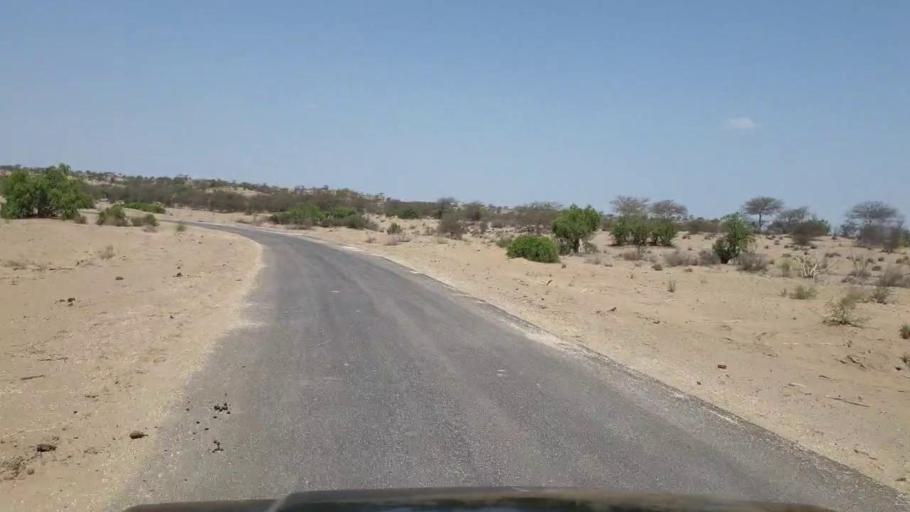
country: PK
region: Sindh
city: Nabisar
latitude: 25.0605
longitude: 69.7906
